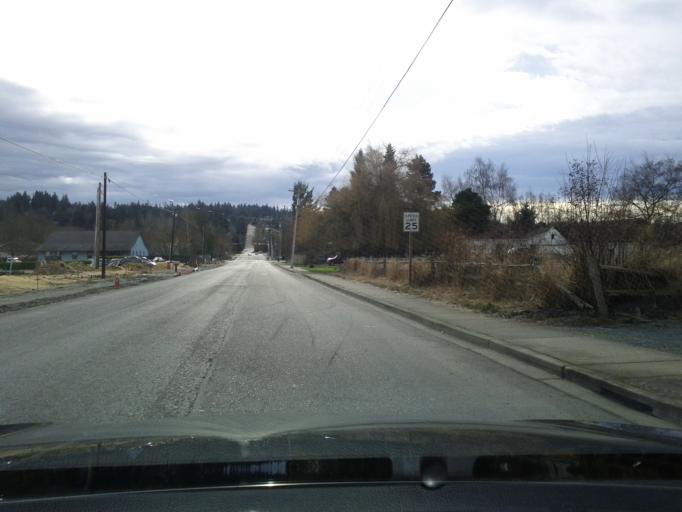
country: US
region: Washington
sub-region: Skagit County
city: Mount Vernon
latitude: 48.4385
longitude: -122.2918
